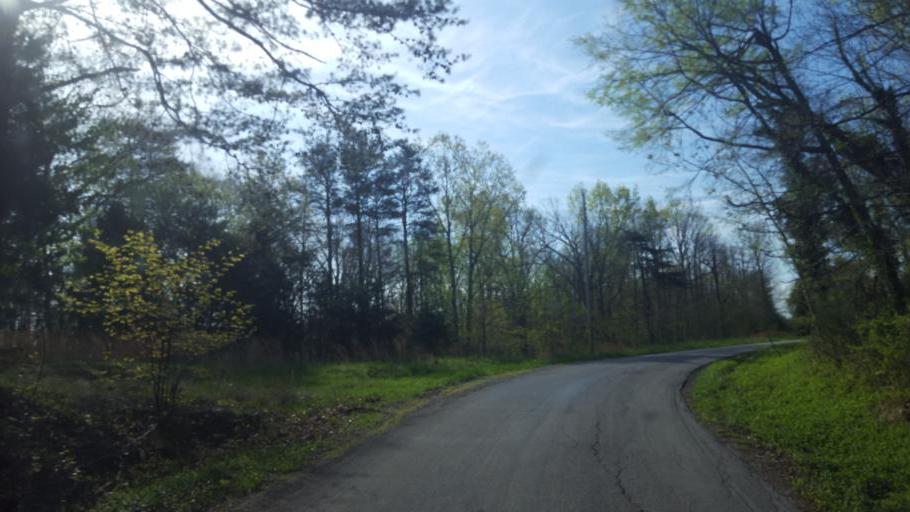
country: US
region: Kentucky
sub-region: Hart County
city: Munfordville
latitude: 37.3262
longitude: -86.0963
